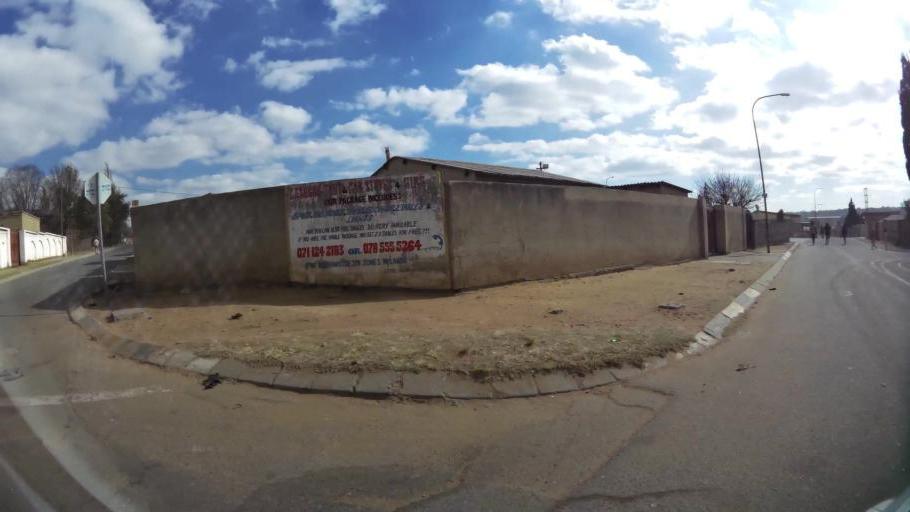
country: ZA
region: Gauteng
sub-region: City of Johannesburg Metropolitan Municipality
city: Roodepoort
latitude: -26.2143
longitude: 27.9082
